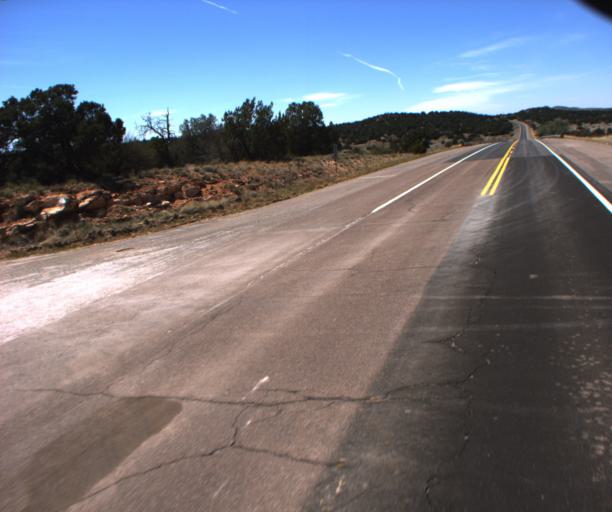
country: US
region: Arizona
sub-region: Mohave County
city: Peach Springs
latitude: 35.5200
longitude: -113.2047
